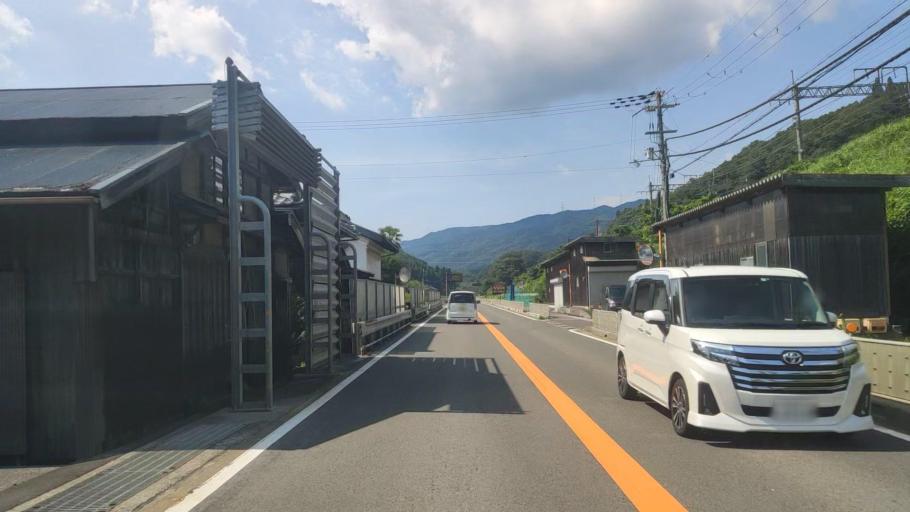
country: JP
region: Fukui
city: Tsuruga
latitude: 35.5393
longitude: 136.1509
